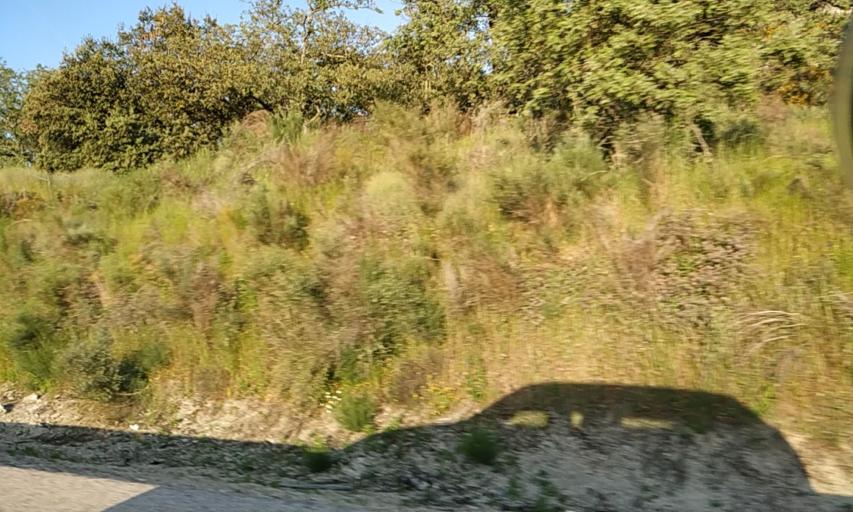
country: ES
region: Extremadura
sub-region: Provincia de Caceres
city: Valencia de Alcantara
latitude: 39.3831
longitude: -7.2480
